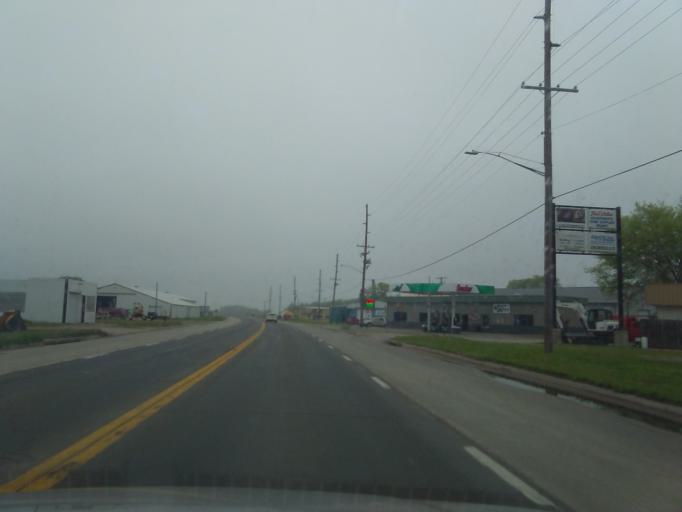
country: US
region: Nebraska
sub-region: Cuming County
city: Wisner
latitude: 41.9290
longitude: -96.8128
